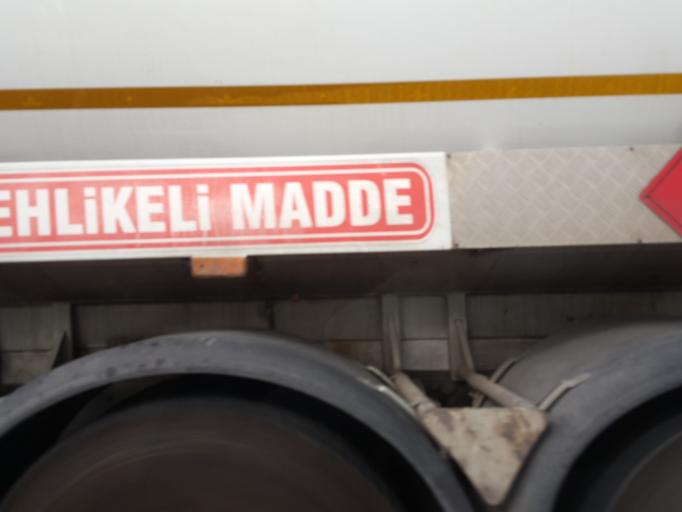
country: TR
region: Kirikkale
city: Bahsili
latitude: 39.7097
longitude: 33.4276
